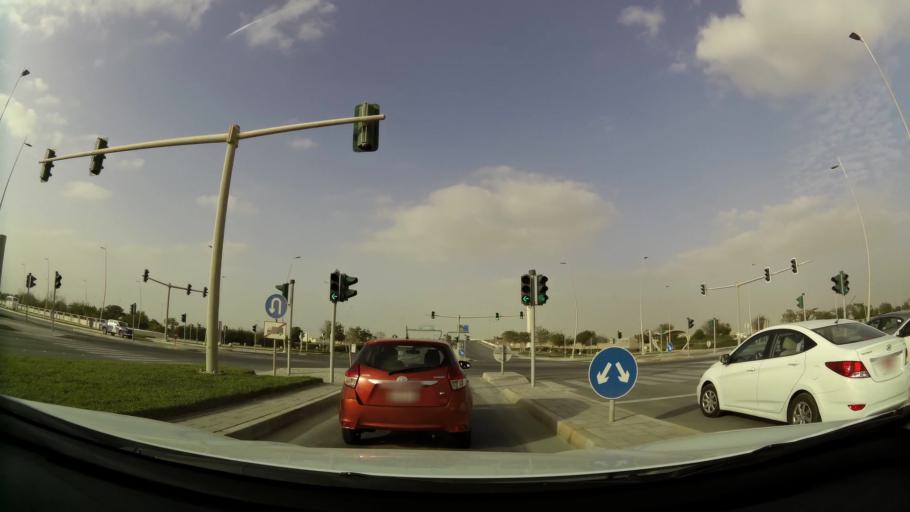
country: AE
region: Abu Dhabi
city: Abu Dhabi
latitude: 24.4957
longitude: 54.5912
